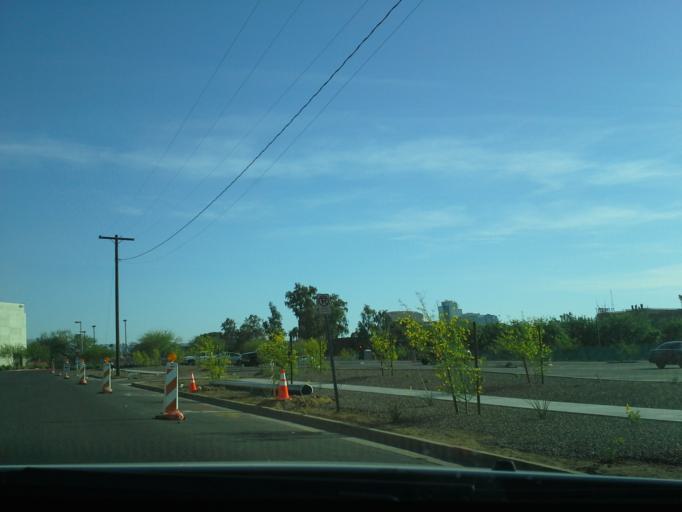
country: US
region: Arizona
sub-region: Maricopa County
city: Phoenix
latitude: 33.4647
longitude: -112.0620
